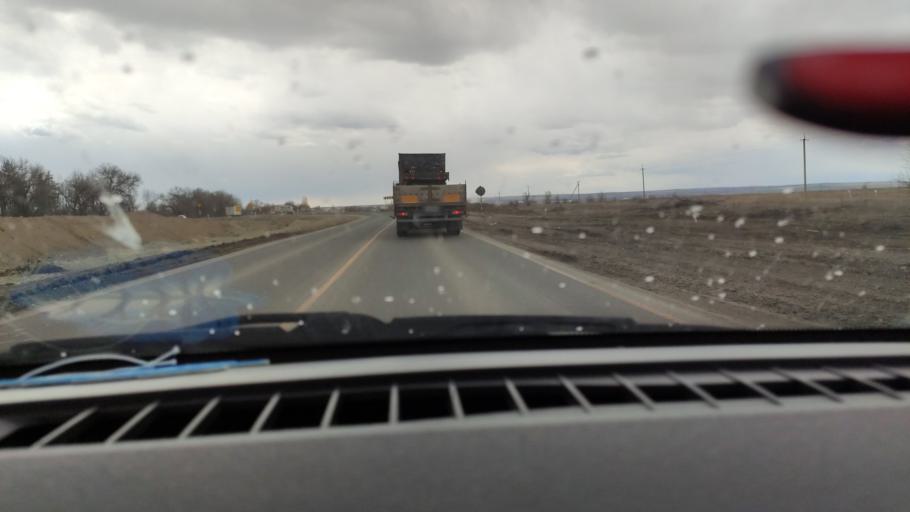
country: RU
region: Saratov
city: Sinodskoye
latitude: 52.0049
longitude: 46.6828
